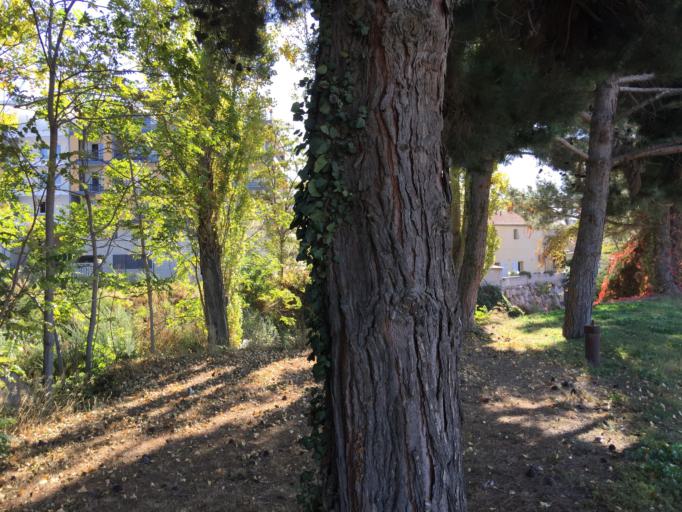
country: FR
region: Provence-Alpes-Cote d'Azur
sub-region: Departement des Bouches-du-Rhone
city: Marseille 10
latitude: 43.2823
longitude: 5.4203
